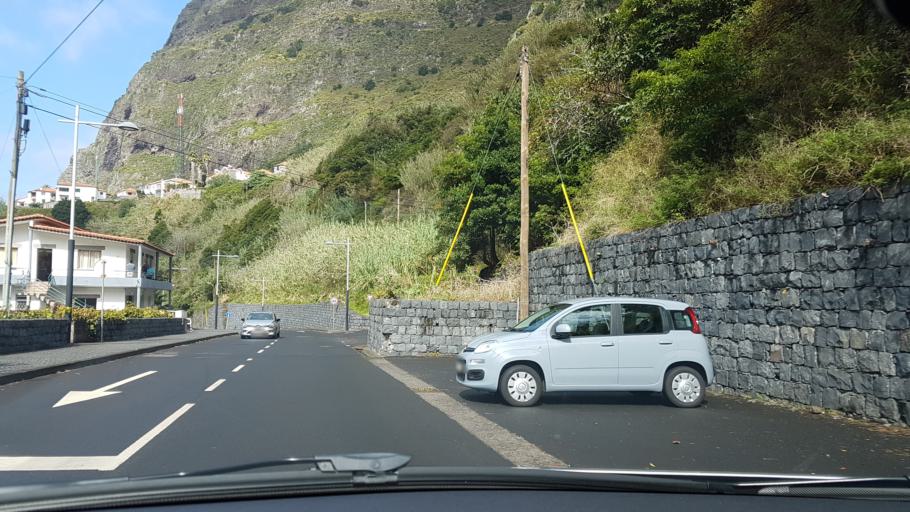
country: PT
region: Madeira
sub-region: Sao Vicente
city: Sao Vicente
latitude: 32.8008
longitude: -17.0423
